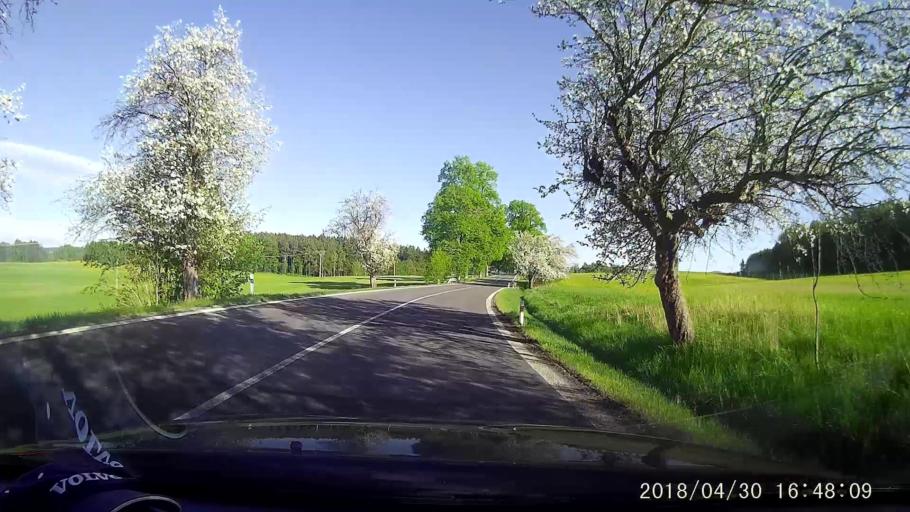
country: CZ
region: Liberecky
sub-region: Okres Liberec
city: Frydlant
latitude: 50.9735
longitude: 15.0884
